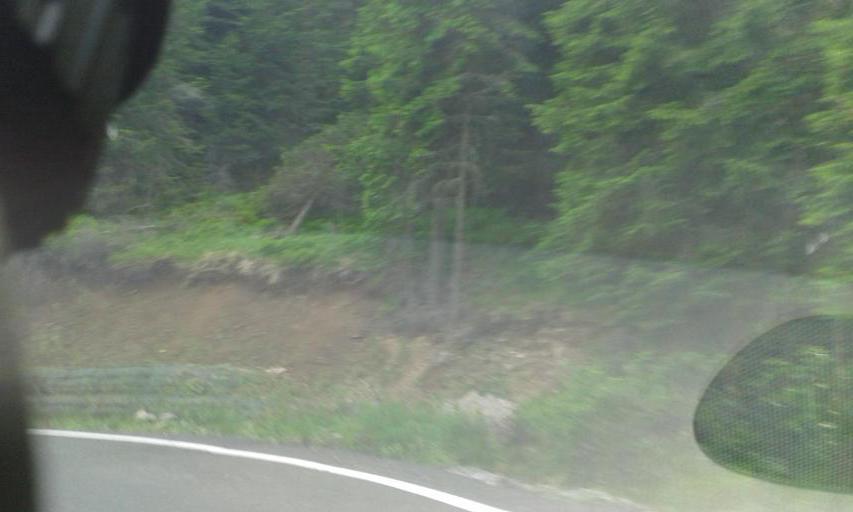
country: RO
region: Hunedoara
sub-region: Oras Petrila
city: Petrila
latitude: 45.5048
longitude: 23.6424
